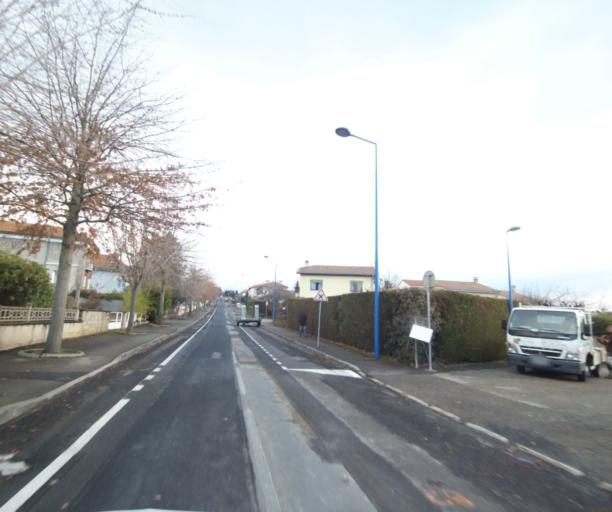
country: FR
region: Rhone-Alpes
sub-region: Departement de la Loire
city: La Talaudiere
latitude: 45.4823
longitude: 4.4313
